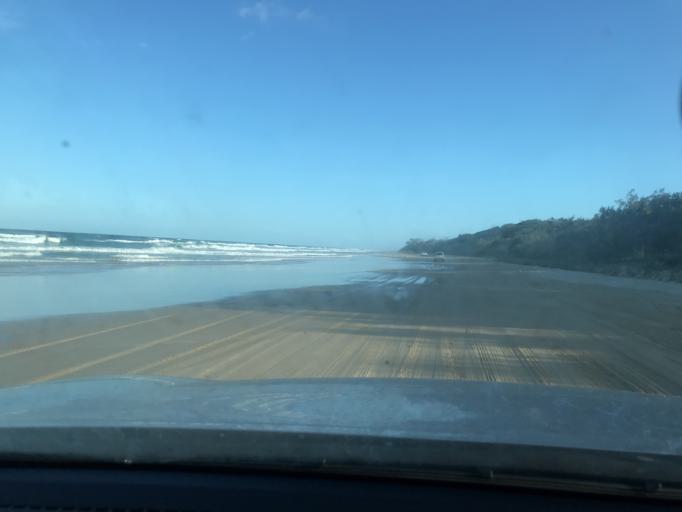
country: AU
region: Queensland
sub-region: Fraser Coast
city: Urangan
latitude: -25.4116
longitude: 153.1699
